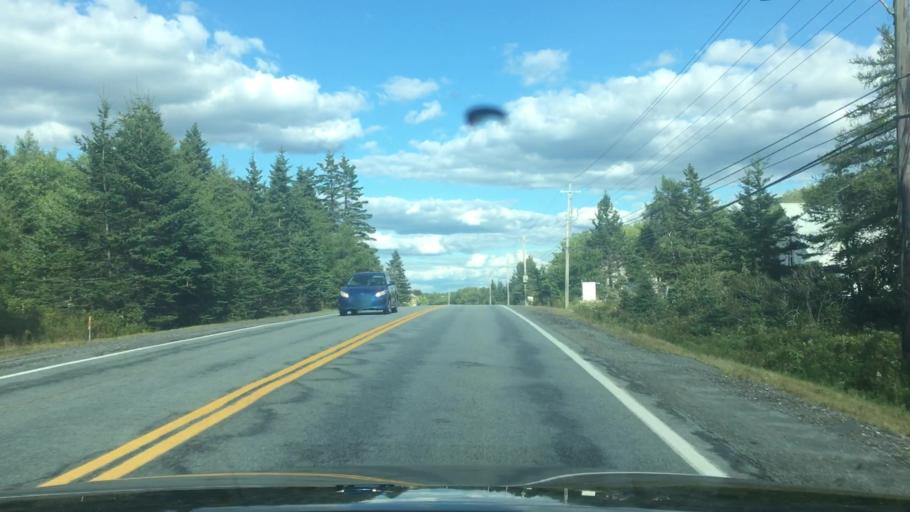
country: CA
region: Nova Scotia
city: Halifax
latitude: 44.5973
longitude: -63.6917
